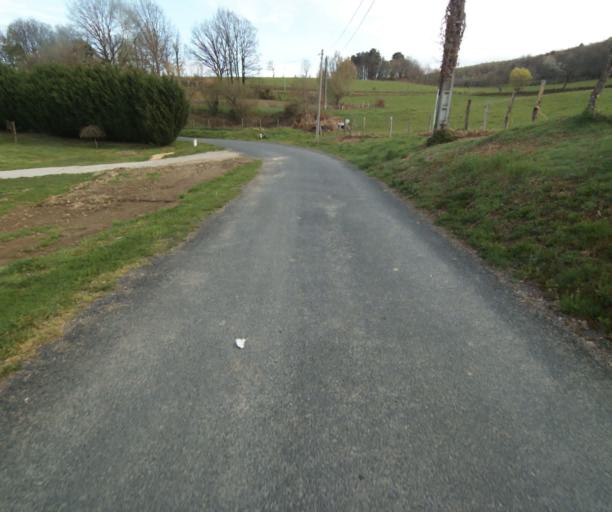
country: FR
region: Limousin
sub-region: Departement de la Correze
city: Correze
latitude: 45.3563
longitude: 1.8444
